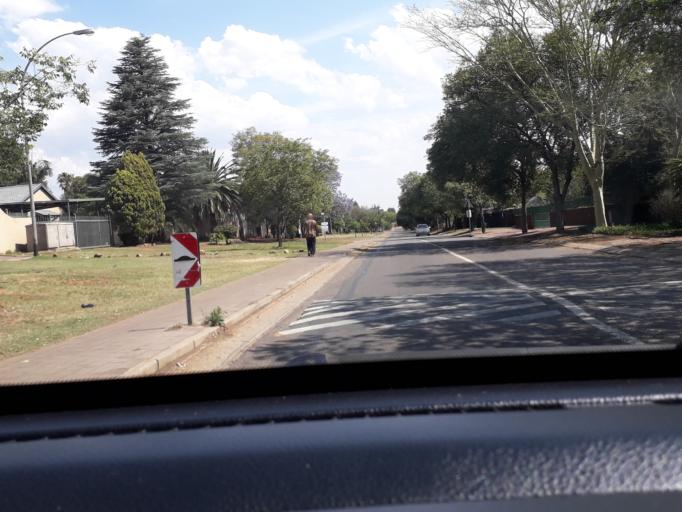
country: ZA
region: Gauteng
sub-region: City of Tshwane Metropolitan Municipality
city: Centurion
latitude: -25.8410
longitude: 28.2385
